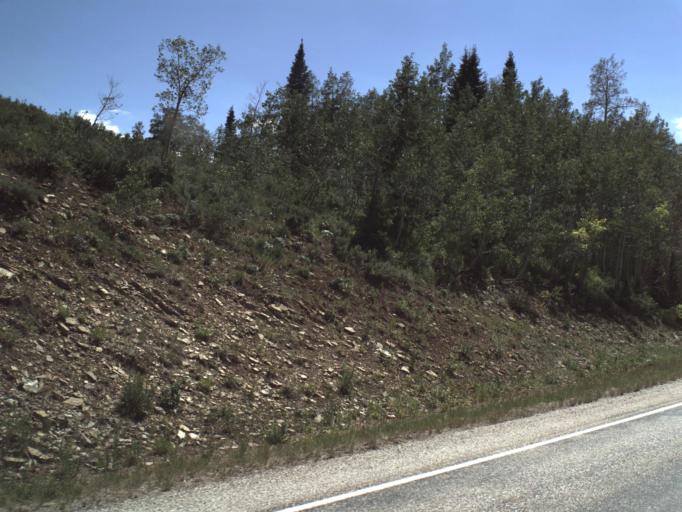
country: US
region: Utah
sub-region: Rich County
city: Randolph
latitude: 41.4766
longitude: -111.4568
